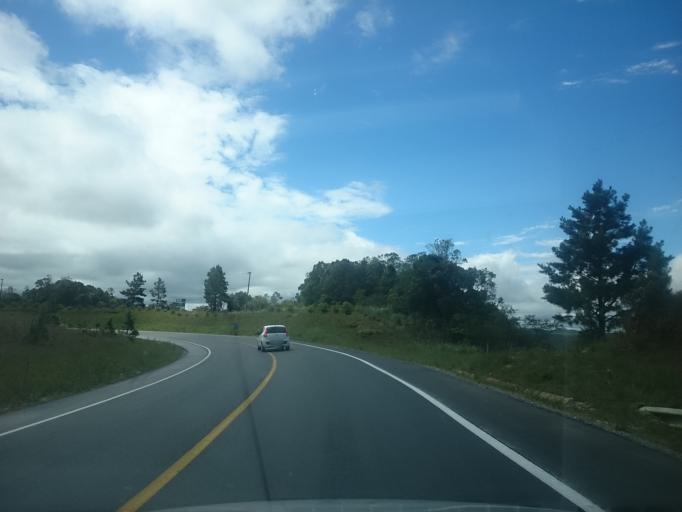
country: BR
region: Santa Catarina
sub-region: Anitapolis
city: Anitapolis
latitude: -27.6643
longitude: -49.1594
